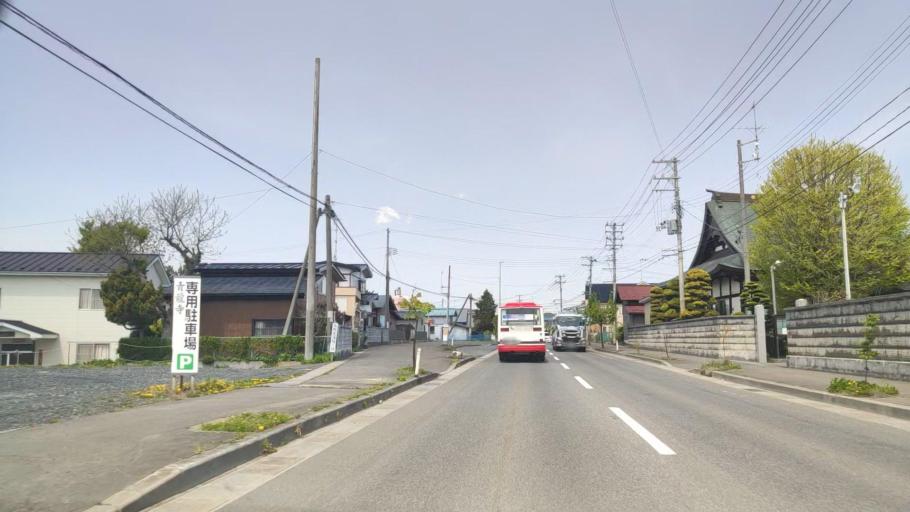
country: JP
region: Aomori
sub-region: Hachinohe Shi
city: Uchimaru
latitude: 40.5047
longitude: 141.4391
